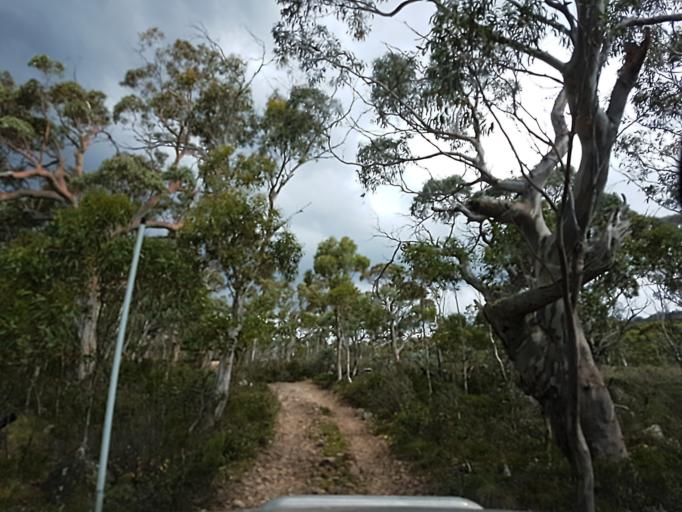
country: AU
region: New South Wales
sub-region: Snowy River
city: Jindabyne
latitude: -36.8760
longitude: 148.1783
